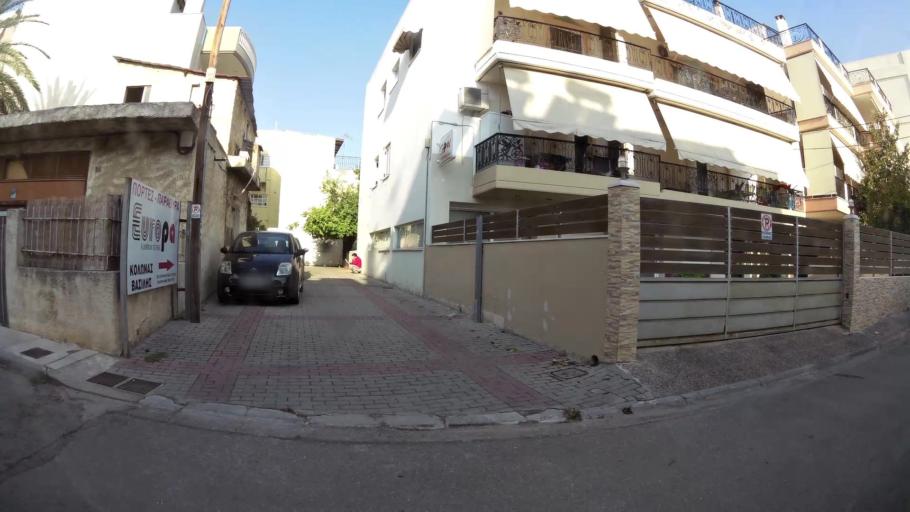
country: GR
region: Attica
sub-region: Nomarchia Athinas
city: Nea Filadelfeia
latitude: 38.0529
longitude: 23.7342
